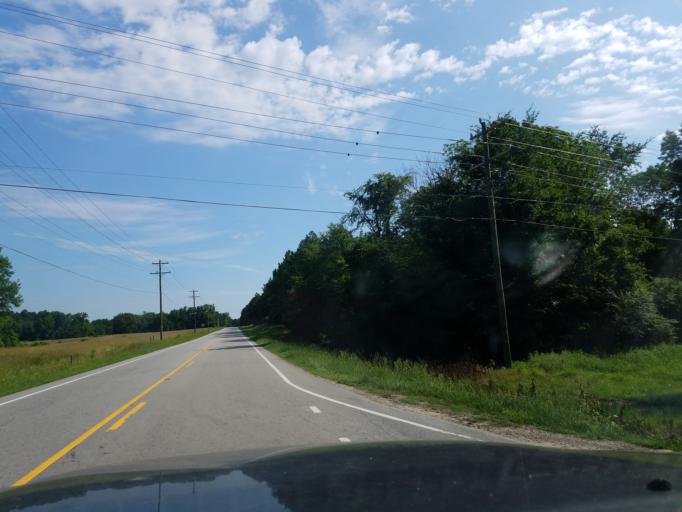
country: US
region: North Carolina
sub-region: Vance County
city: Henderson
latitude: 36.3754
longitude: -78.4174
